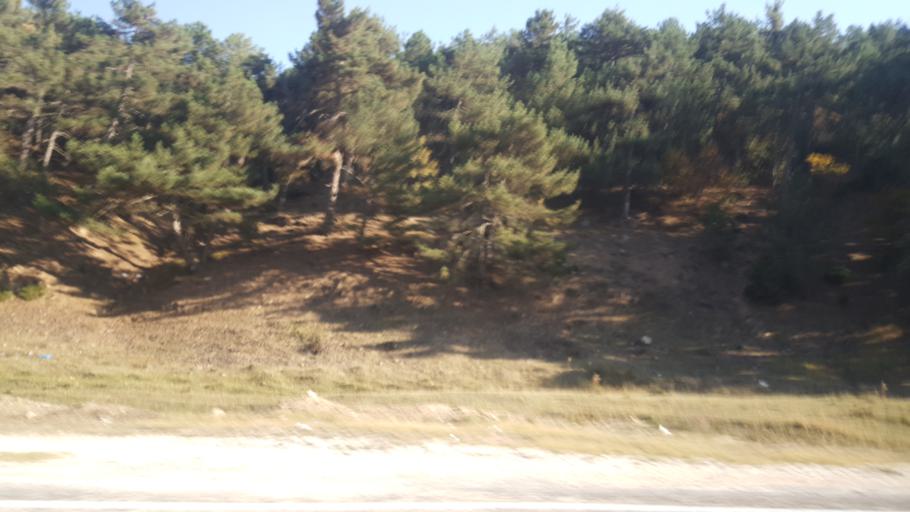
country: TR
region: Eskisehir
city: Kirka
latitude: 39.1083
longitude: 30.5836
